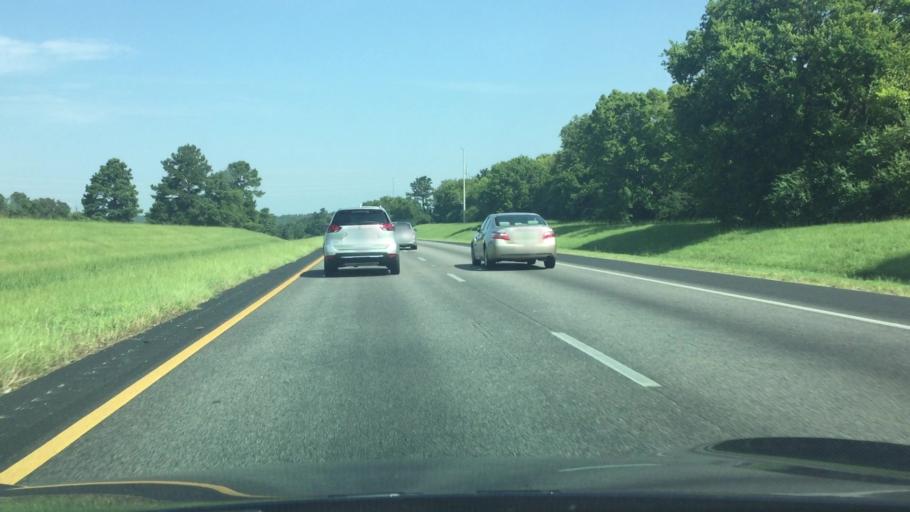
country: US
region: Alabama
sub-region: Autauga County
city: Prattville
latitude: 32.5062
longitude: -86.4211
